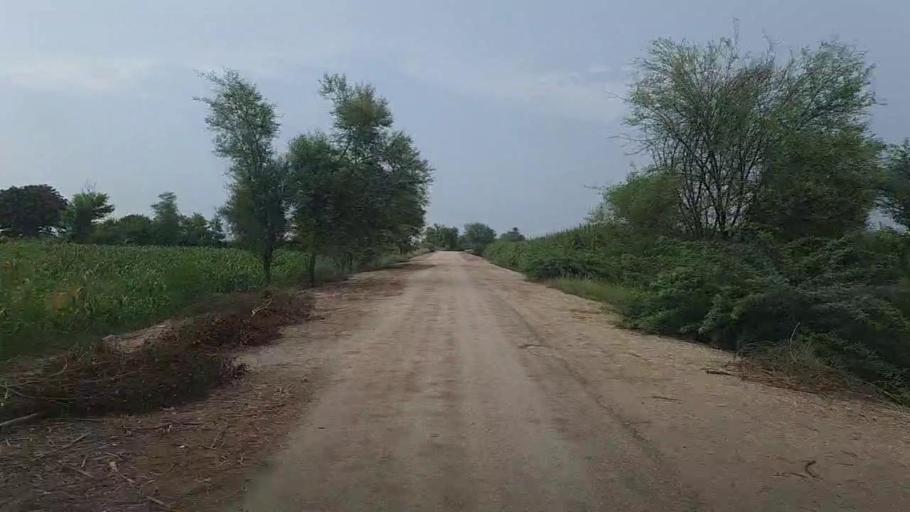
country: PK
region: Sindh
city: Karaundi
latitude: 26.9754
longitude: 68.4288
